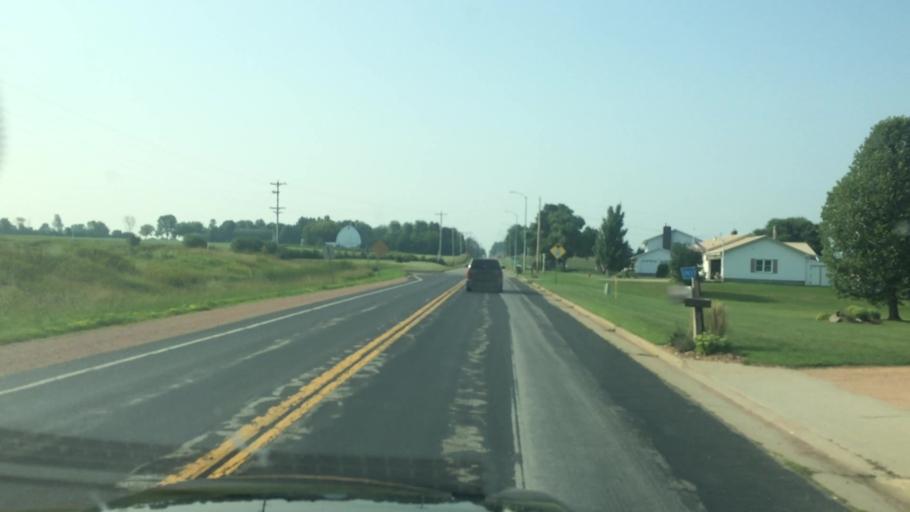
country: US
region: Wisconsin
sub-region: Marathon County
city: Stratford
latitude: 44.8163
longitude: -90.0792
